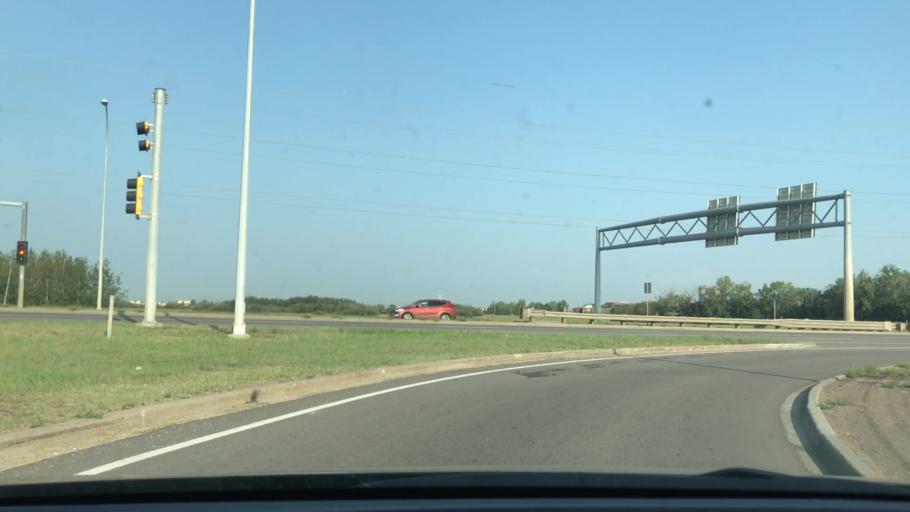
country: CA
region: Alberta
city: Beaumont
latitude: 53.4398
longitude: -113.4661
